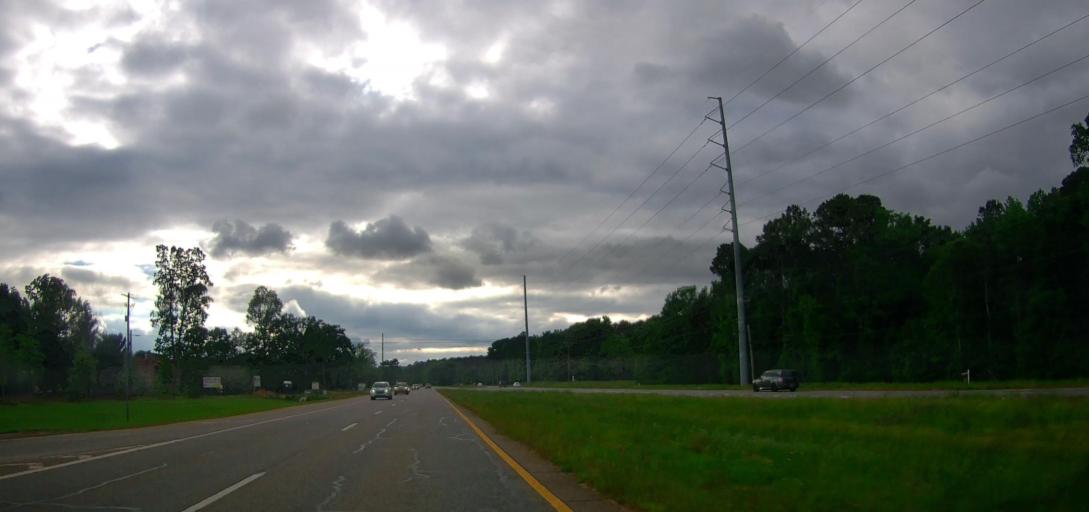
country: US
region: Georgia
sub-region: Oconee County
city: Bogart
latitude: 33.9183
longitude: -83.5276
